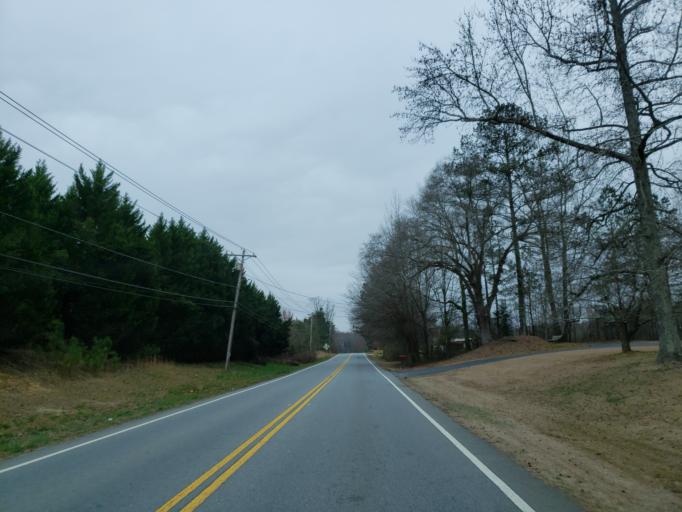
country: US
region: Georgia
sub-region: Cobb County
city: Powder Springs
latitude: 33.9257
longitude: -84.6412
